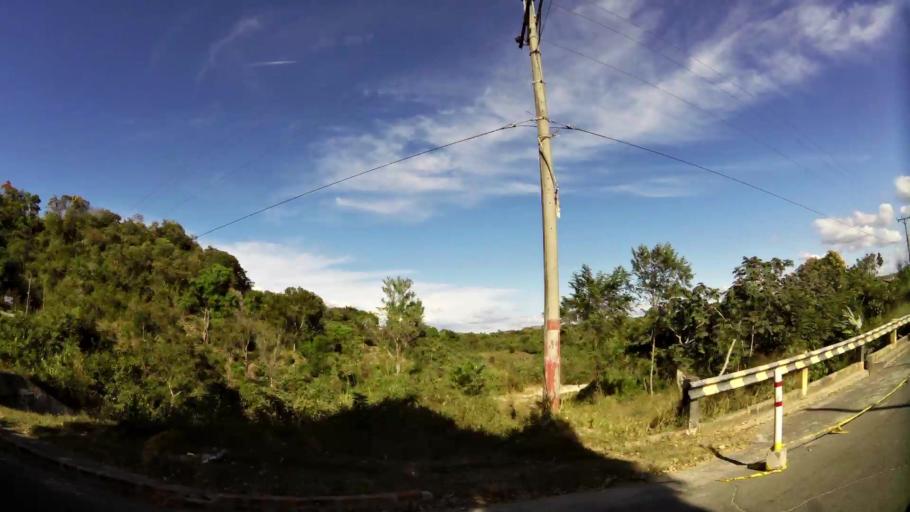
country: SV
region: Cuscatlan
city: Tecoluca
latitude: 13.8294
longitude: -89.0311
